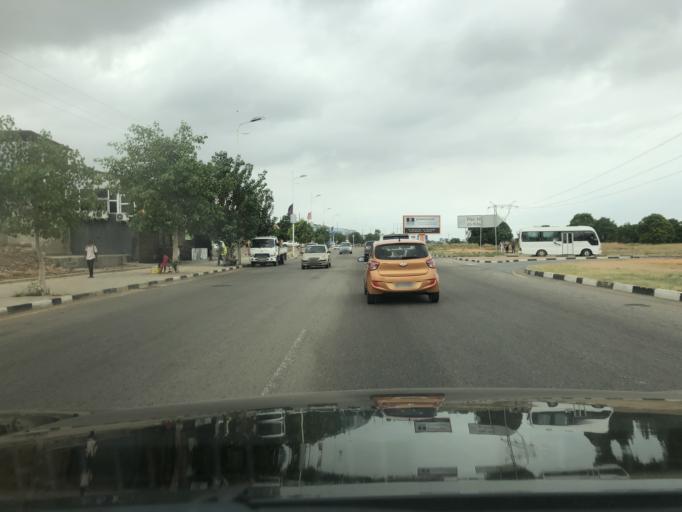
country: AO
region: Luanda
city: Luanda
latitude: -8.9753
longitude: 13.2893
